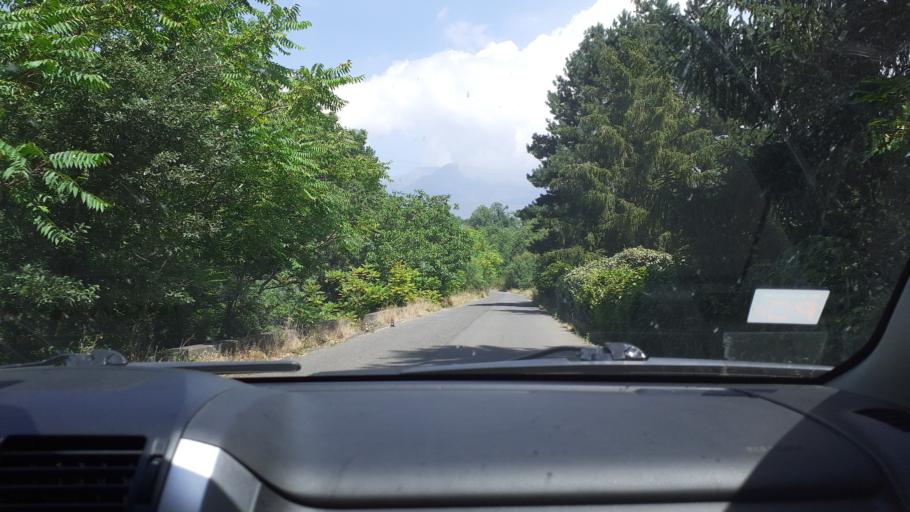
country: IT
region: Sicily
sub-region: Catania
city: Nicolosi
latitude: 37.6376
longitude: 15.0219
